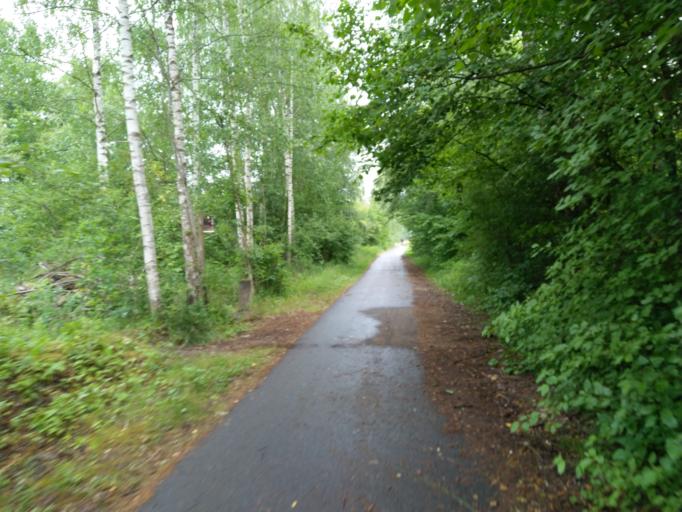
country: BE
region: Wallonia
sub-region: Province de Namur
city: Anhee
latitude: 50.3174
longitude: 4.8409
